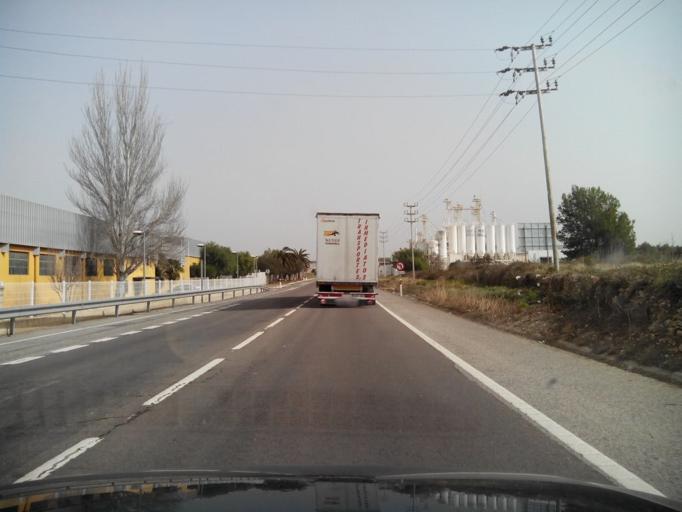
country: ES
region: Catalonia
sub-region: Provincia de Tarragona
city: Santa Oliva
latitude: 41.2311
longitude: 1.5593
